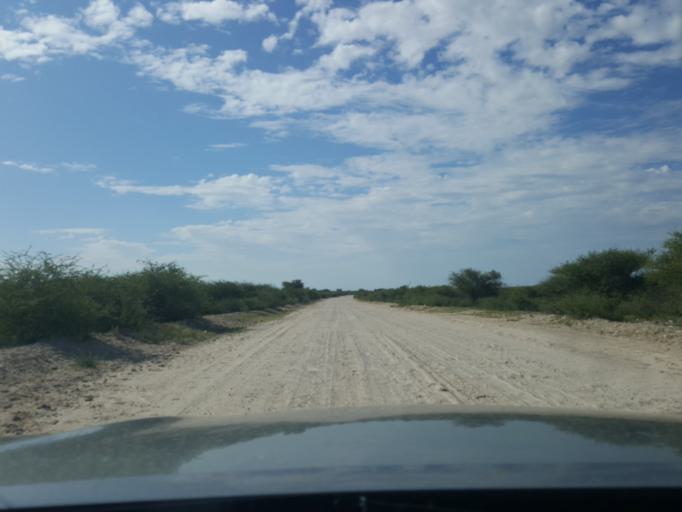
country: BW
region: Kweneng
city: Khudumelapye
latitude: -23.6033
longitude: 24.7235
